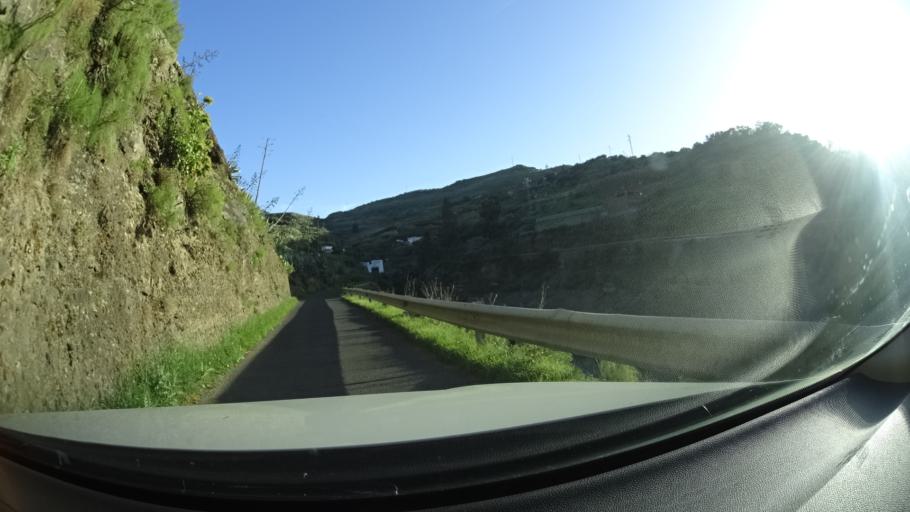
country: ES
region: Canary Islands
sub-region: Provincia de Las Palmas
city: Artenara
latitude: 28.0448
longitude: -15.6712
